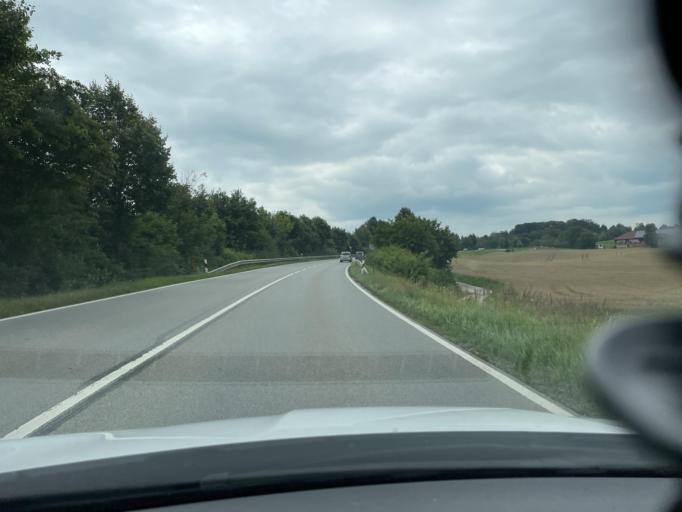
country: DE
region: Bavaria
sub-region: Upper Bavaria
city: Soyen
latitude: 48.1274
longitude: 12.1851
